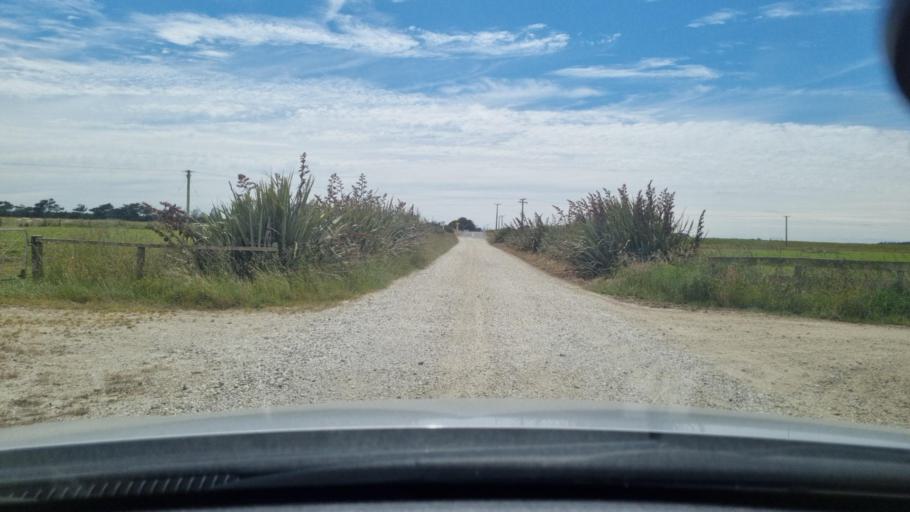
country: NZ
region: Southland
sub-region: Invercargill City
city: Invercargill
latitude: -46.3932
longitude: 168.2720
